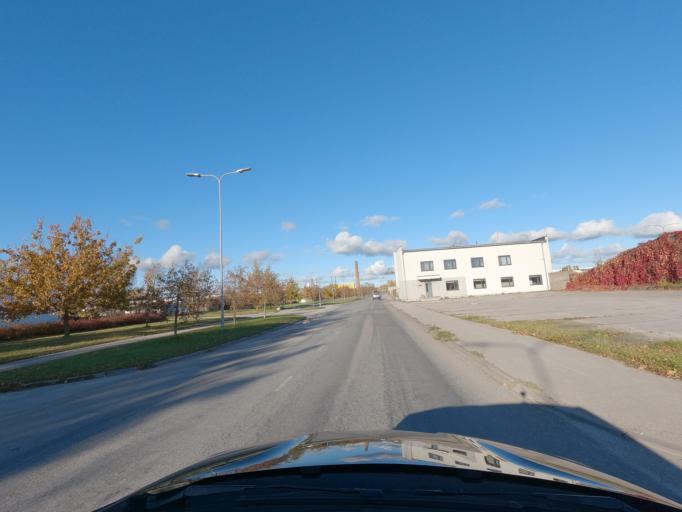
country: EE
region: Saare
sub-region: Kuressaare linn
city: Kuressaare
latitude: 58.2654
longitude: 22.4875
